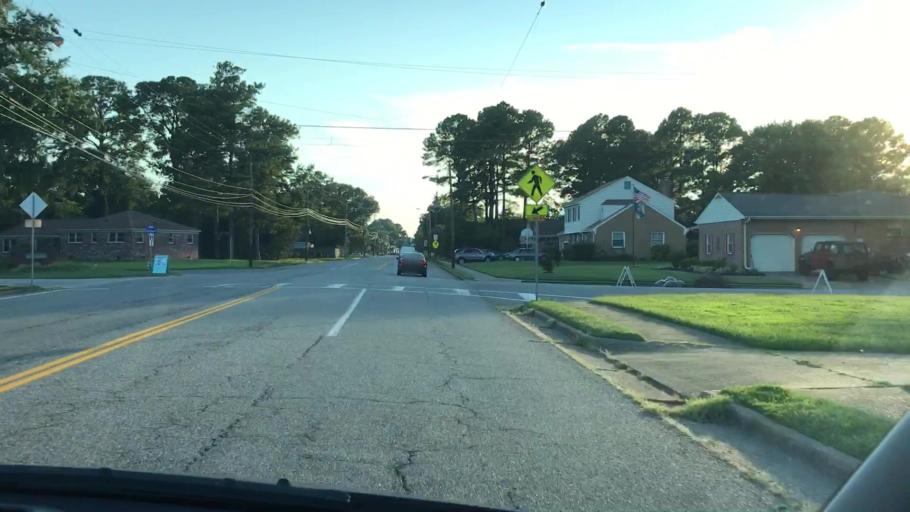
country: US
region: Virginia
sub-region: City of Hampton
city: Hampton
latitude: 37.0579
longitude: -76.3696
